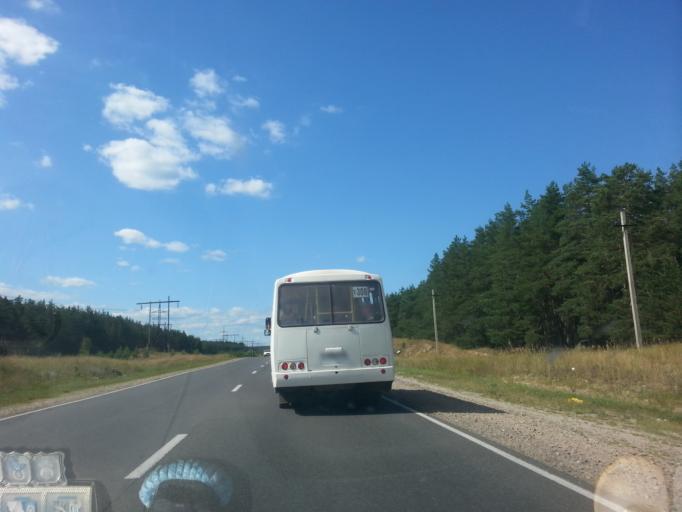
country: RU
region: Nizjnij Novgorod
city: Lukino
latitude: 56.3956
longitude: 43.6776
